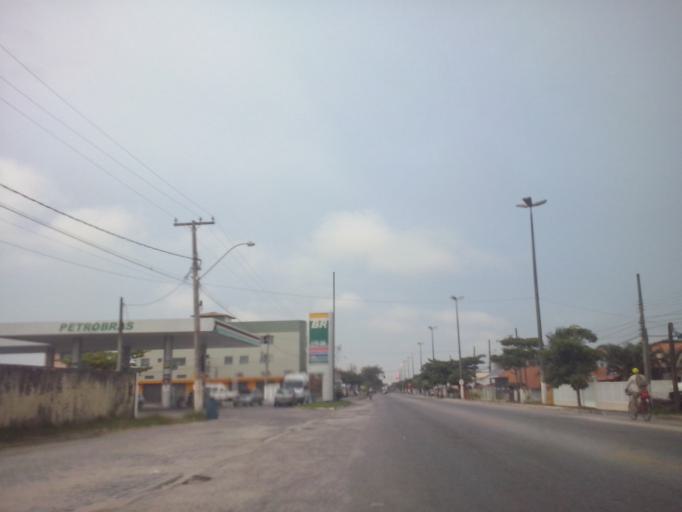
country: BR
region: Rio de Janeiro
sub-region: Rio Das Ostras
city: Rio das Ostras
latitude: -22.5759
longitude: -41.9868
